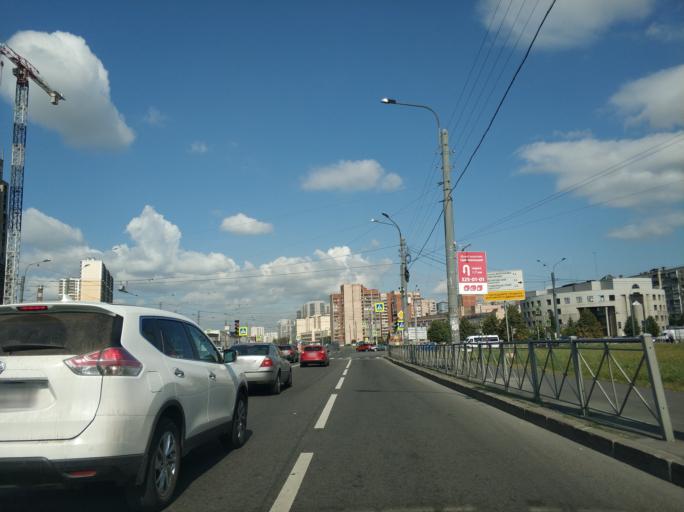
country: RU
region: St.-Petersburg
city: Obukhovo
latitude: 59.9003
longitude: 30.4592
